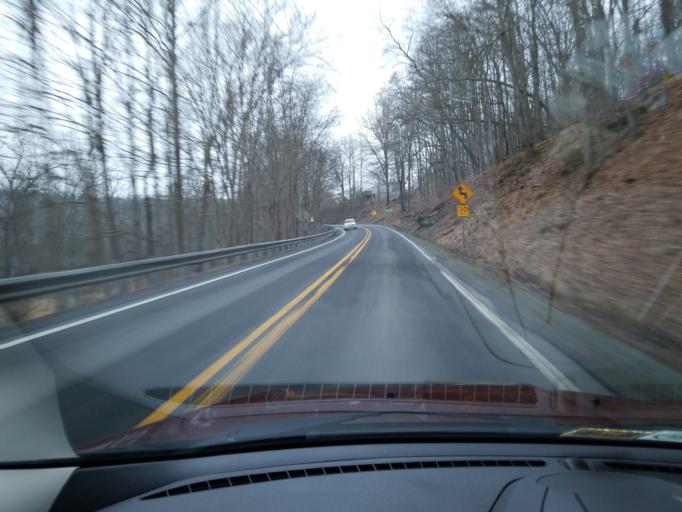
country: US
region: West Virginia
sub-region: Monroe County
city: Union
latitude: 37.5686
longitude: -80.5706
